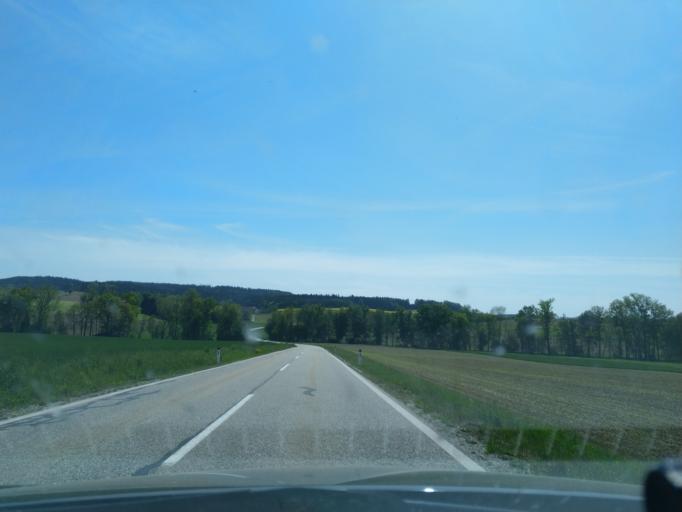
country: DE
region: Bavaria
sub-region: Lower Bavaria
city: Bad Fussing
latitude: 48.2735
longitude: 13.3544
